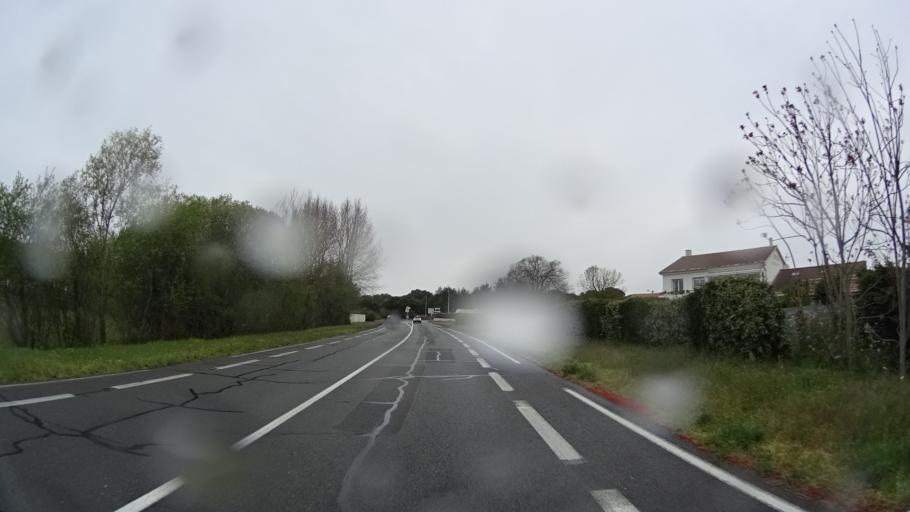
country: FR
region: Pays de la Loire
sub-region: Departement de la Vendee
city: La Barre-de-Monts
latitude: 46.8835
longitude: -2.1227
